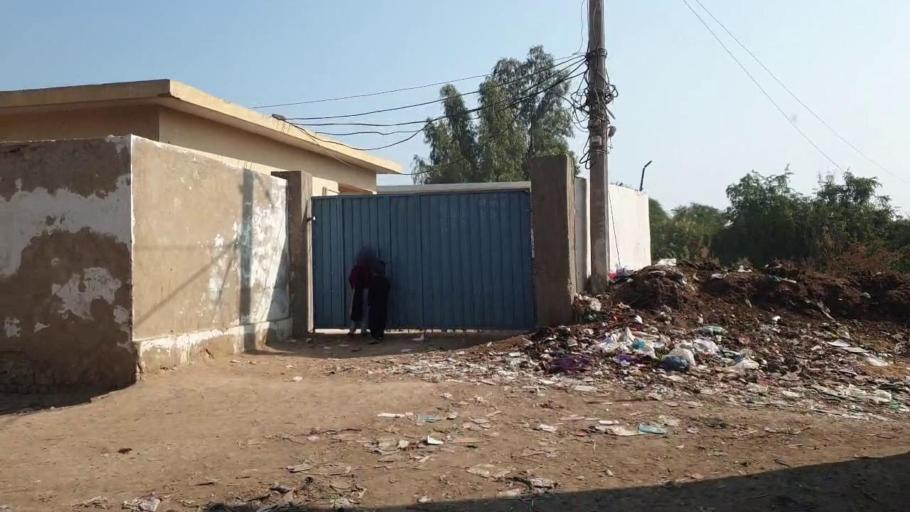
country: PK
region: Sindh
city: Hala
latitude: 25.8902
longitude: 68.4146
